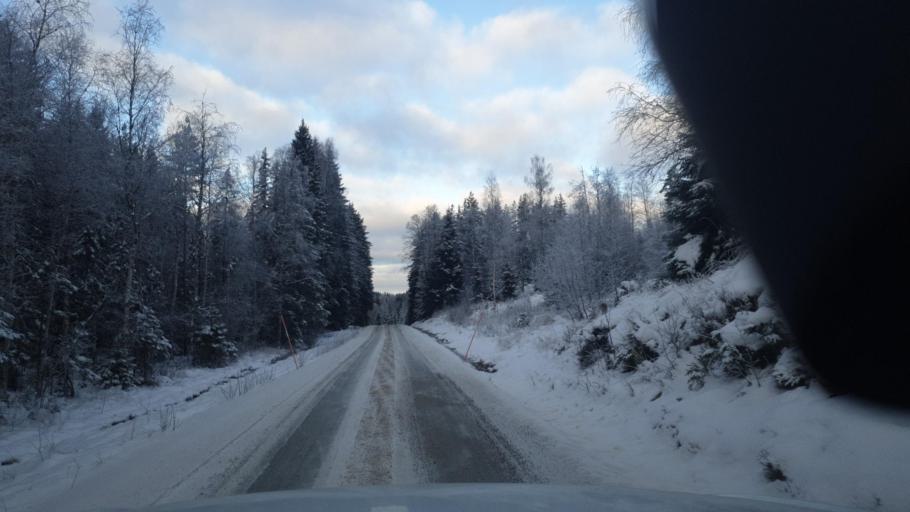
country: SE
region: Vaermland
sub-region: Eda Kommun
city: Charlottenberg
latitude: 60.0526
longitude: 12.6294
